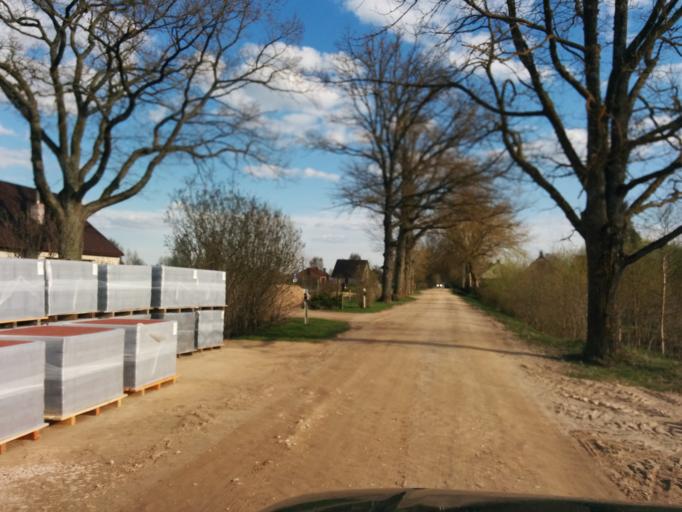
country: LV
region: Jelgava
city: Jelgava
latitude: 56.6662
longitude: 23.6622
